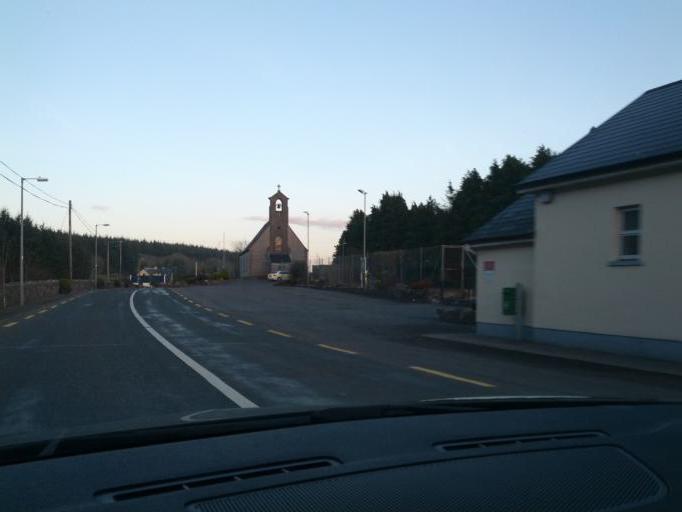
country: IE
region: Connaught
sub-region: Roscommon
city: Boyle
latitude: 53.9749
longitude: -8.4144
